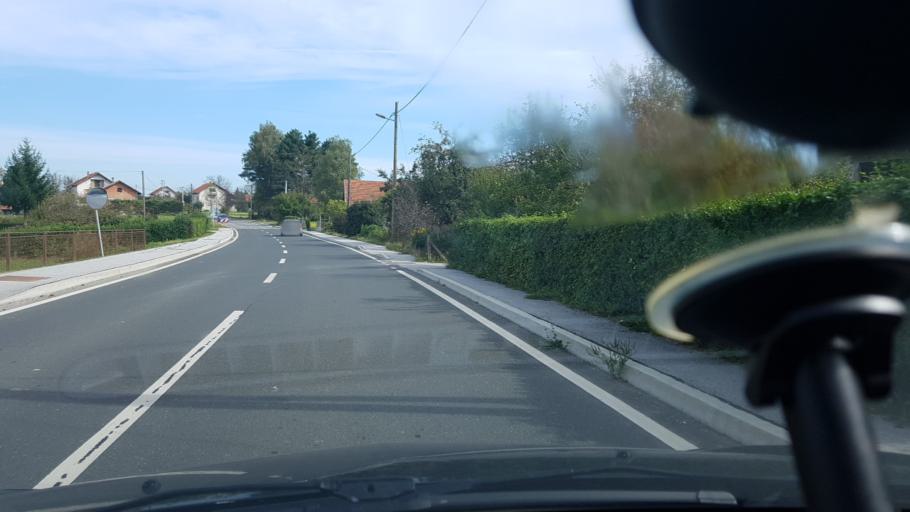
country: HR
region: Krapinsko-Zagorska
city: Marija Bistrica
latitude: 46.0682
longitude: 16.1902
